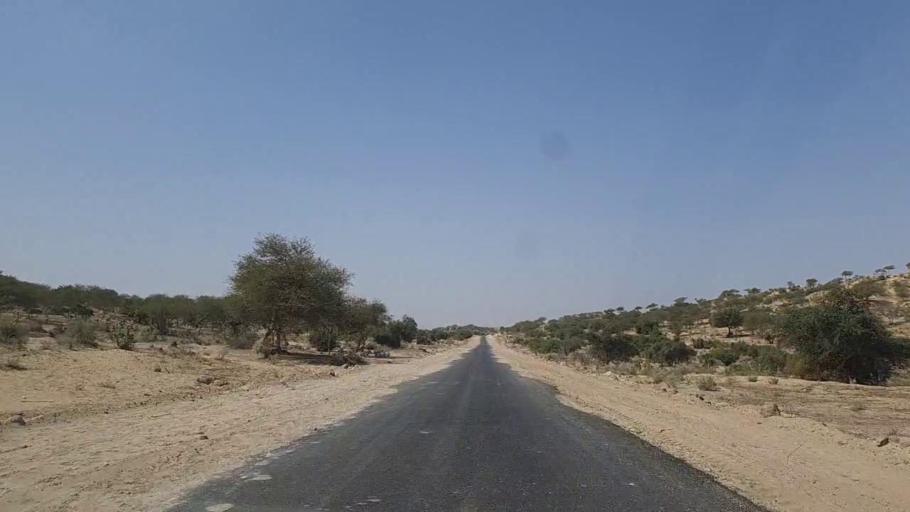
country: PK
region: Sindh
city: Diplo
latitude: 24.5880
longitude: 69.5428
